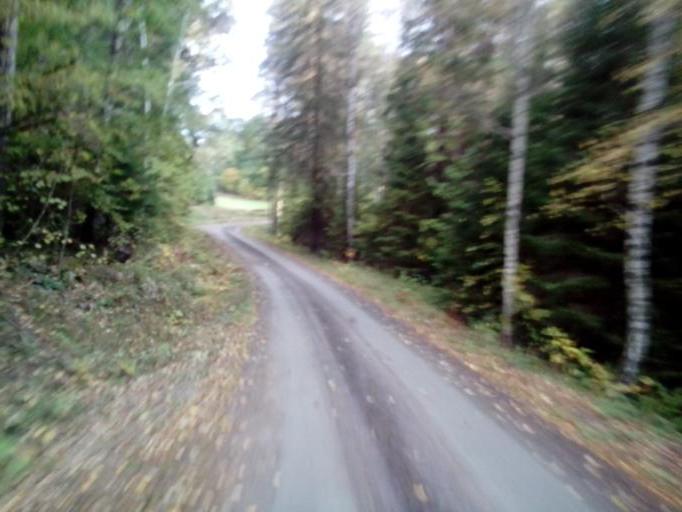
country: SE
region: Kalmar
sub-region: Vasterviks Kommun
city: Overum
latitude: 57.8617
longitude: 16.1258
